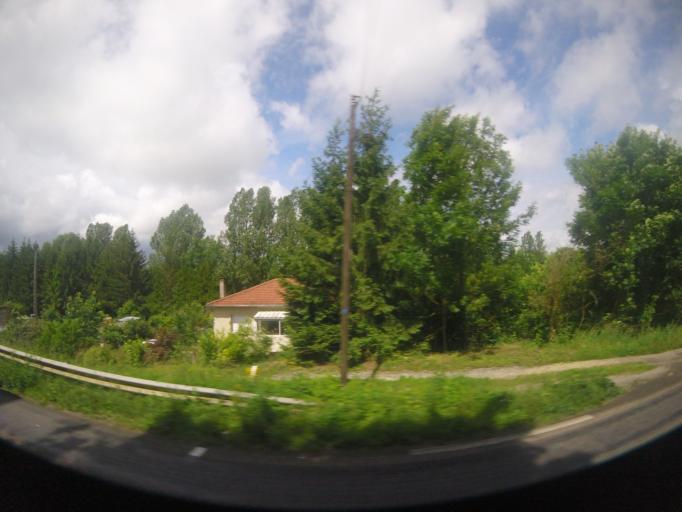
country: FR
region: Lorraine
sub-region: Departement de la Meuse
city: Dugny-sur-Meuse
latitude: 49.1160
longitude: 5.4159
